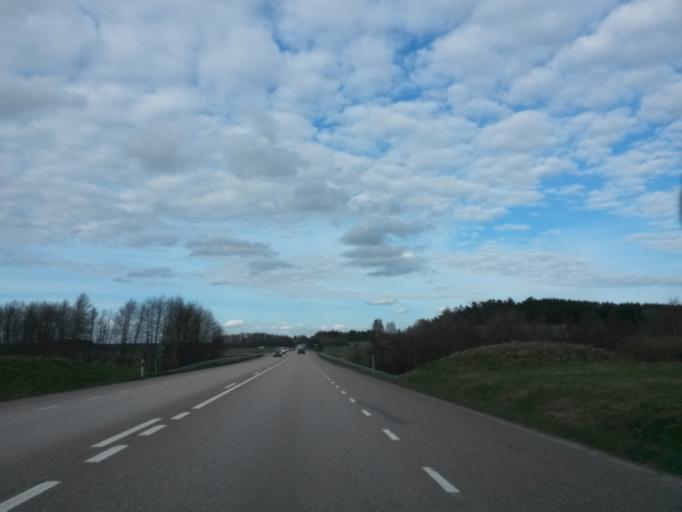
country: SE
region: Vaestra Goetaland
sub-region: Alingsas Kommun
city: Alingsas
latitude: 57.9553
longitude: 12.6094
